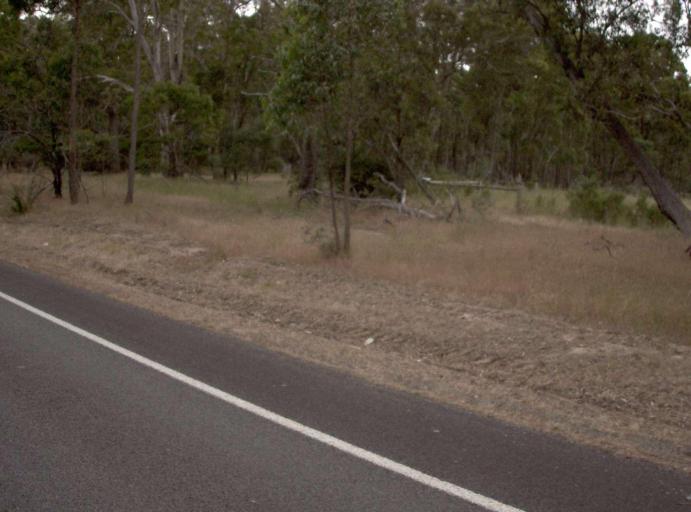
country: AU
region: Victoria
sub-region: Wellington
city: Sale
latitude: -38.4378
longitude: 146.9480
